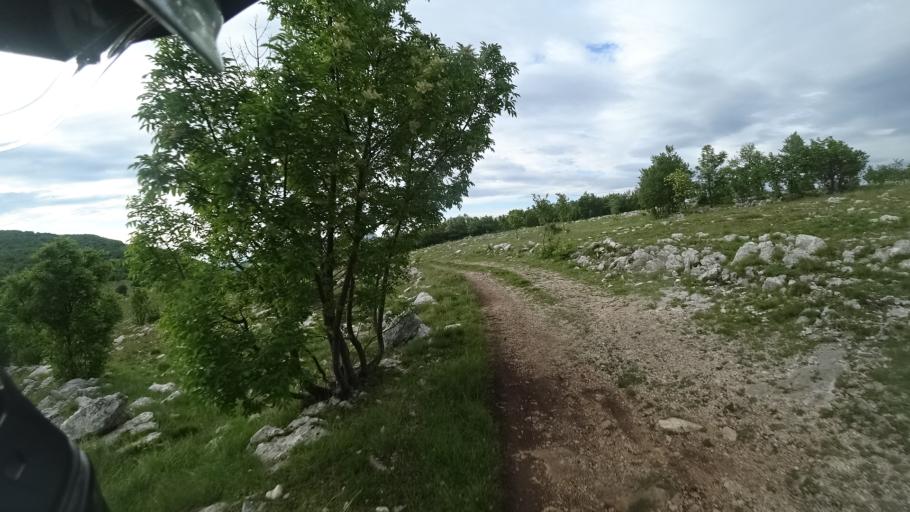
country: HR
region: Sibensko-Kniniska
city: Drnis
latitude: 43.8680
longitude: 16.3907
